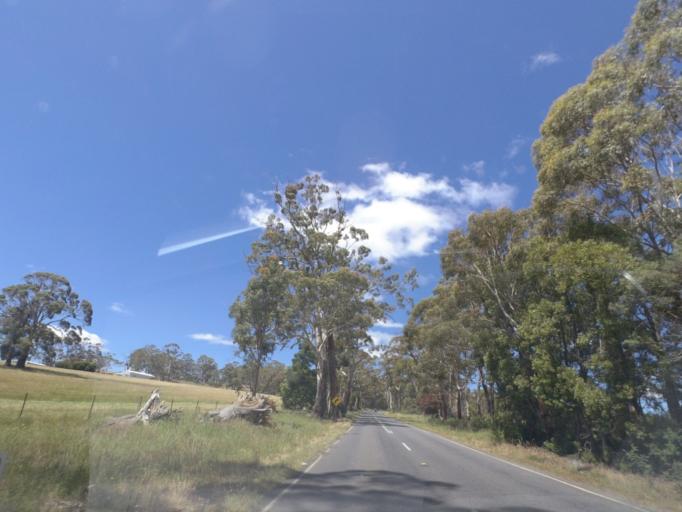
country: AU
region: Victoria
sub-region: Mount Alexander
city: Castlemaine
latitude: -37.2908
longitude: 144.2607
